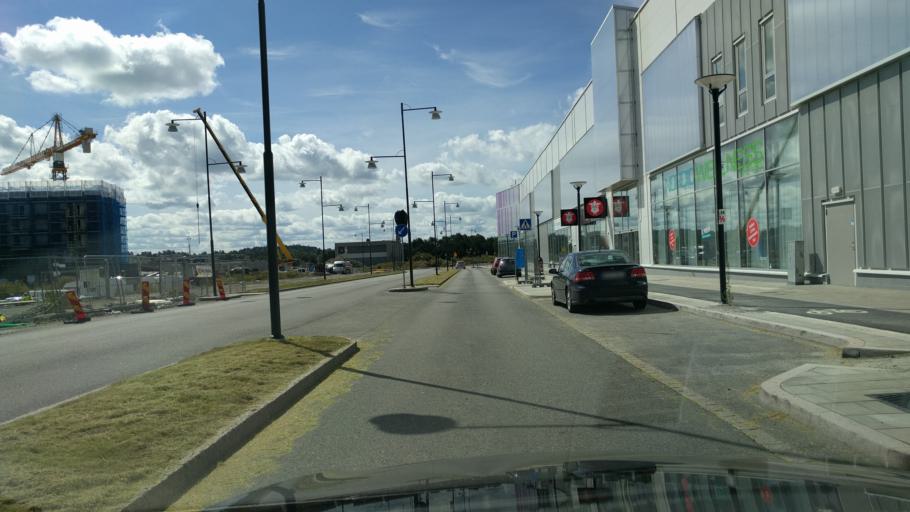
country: SE
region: Stockholm
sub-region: Jarfalla Kommun
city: Jakobsberg
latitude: 59.4127
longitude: 17.8638
